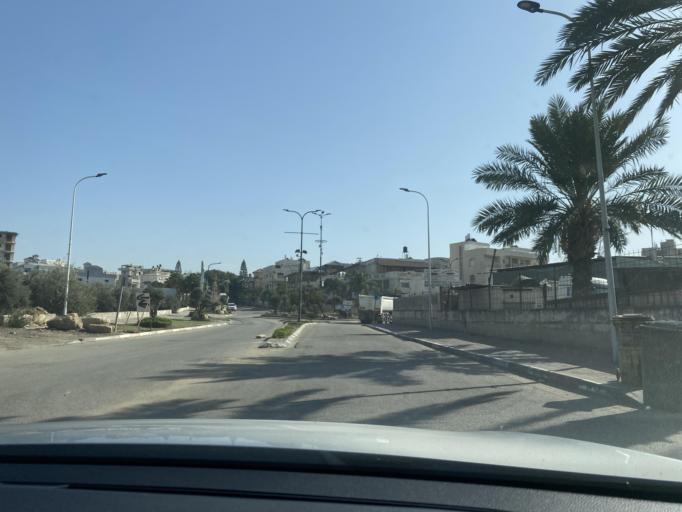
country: IL
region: Central District
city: Kafr Qasim
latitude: 32.1327
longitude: 34.9644
